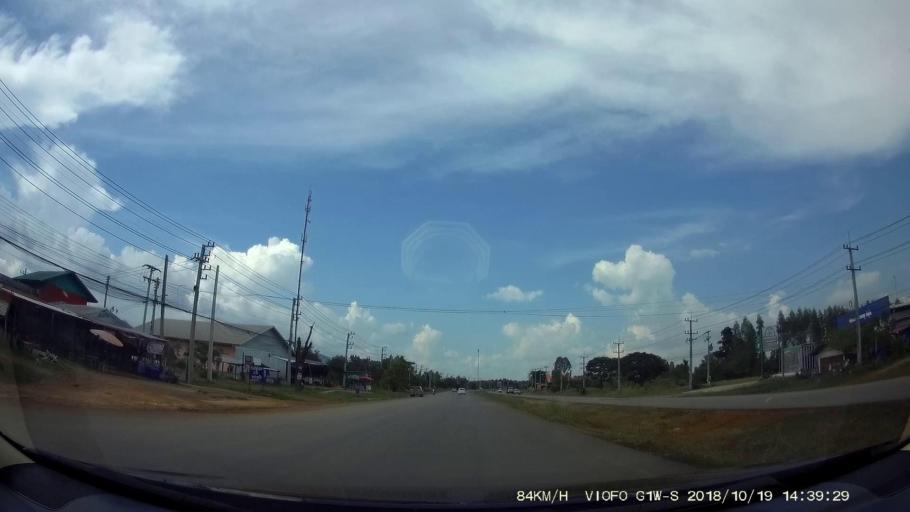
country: TH
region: Chaiyaphum
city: Kaeng Khro
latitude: 16.2266
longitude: 102.1949
